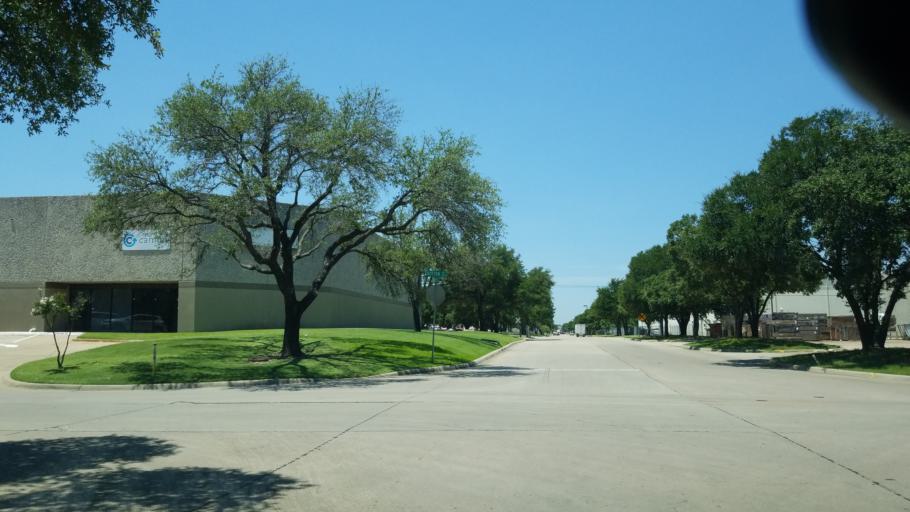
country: US
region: Texas
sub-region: Dallas County
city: Farmers Branch
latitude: 32.9321
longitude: -96.9152
